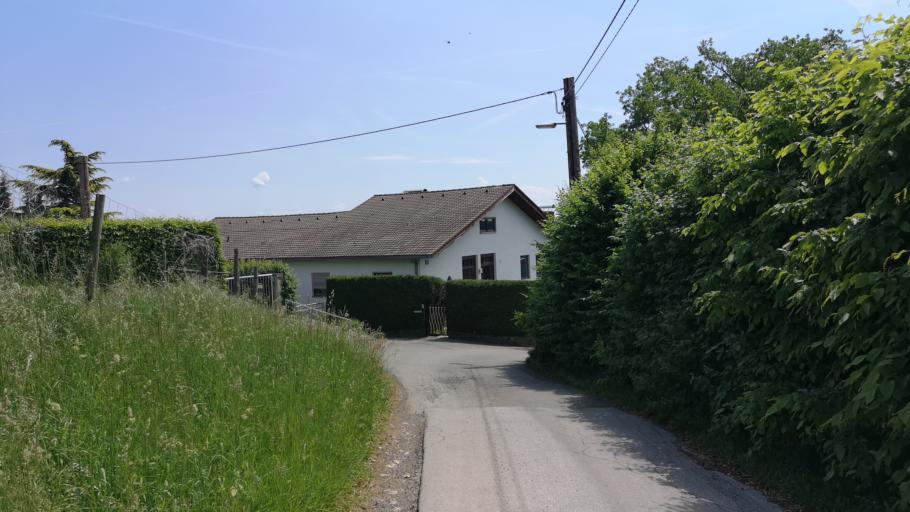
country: AT
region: Styria
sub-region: Graz Stadt
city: Wetzelsdorf
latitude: 47.0321
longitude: 15.3739
